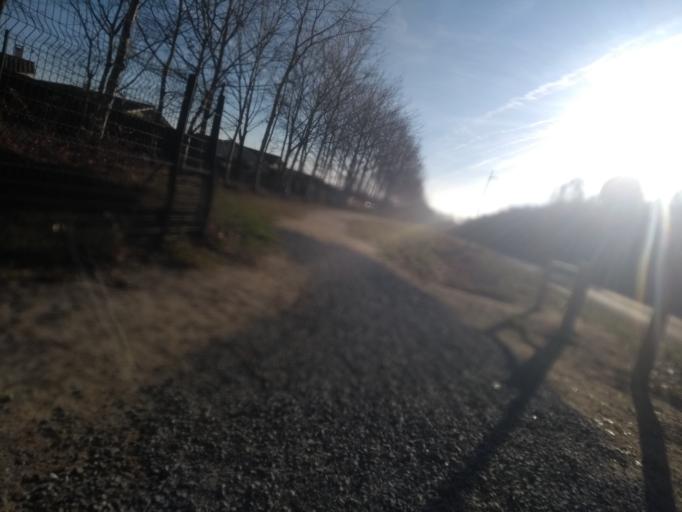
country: FR
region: Aquitaine
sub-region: Departement de la Gironde
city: Le Barp
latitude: 44.6104
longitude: -0.7820
